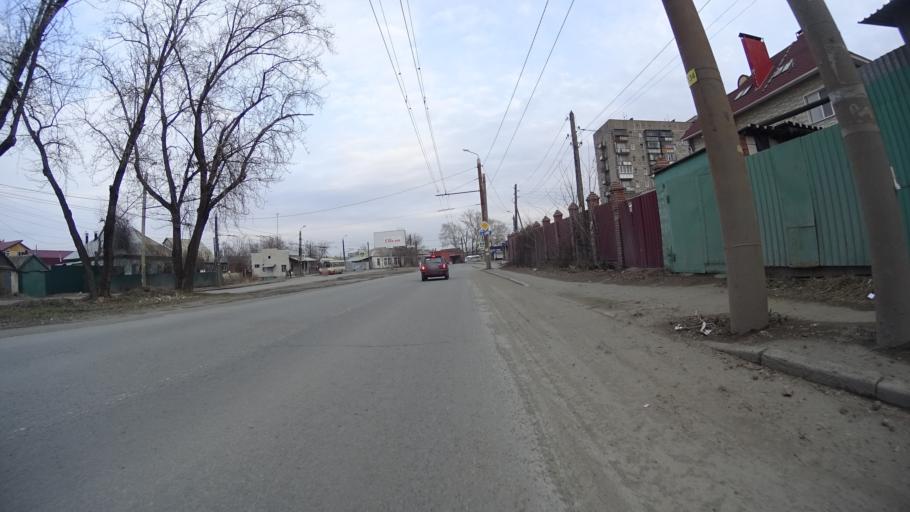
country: RU
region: Chelyabinsk
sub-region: Gorod Chelyabinsk
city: Chelyabinsk
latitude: 55.1908
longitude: 61.4743
